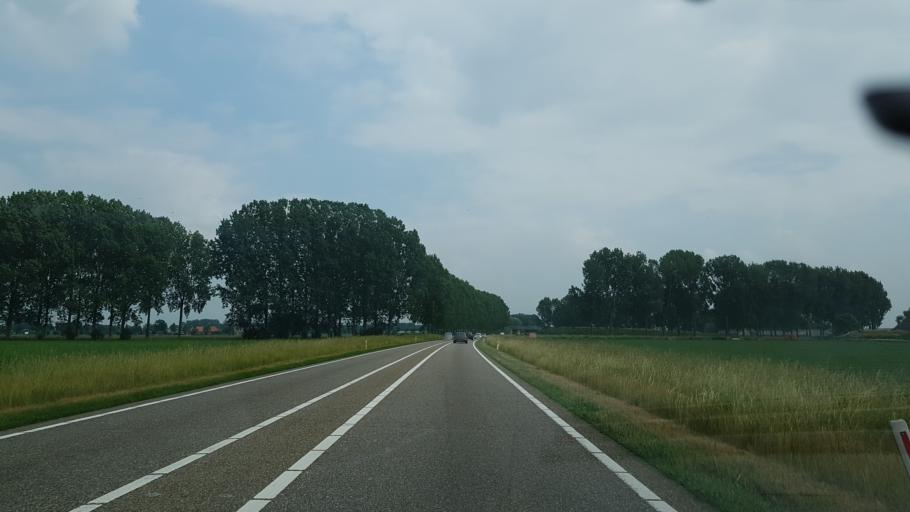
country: NL
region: North Brabant
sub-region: Gemeente Laarbeek
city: Aarle-Rixtel
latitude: 51.5468
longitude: 5.6448
